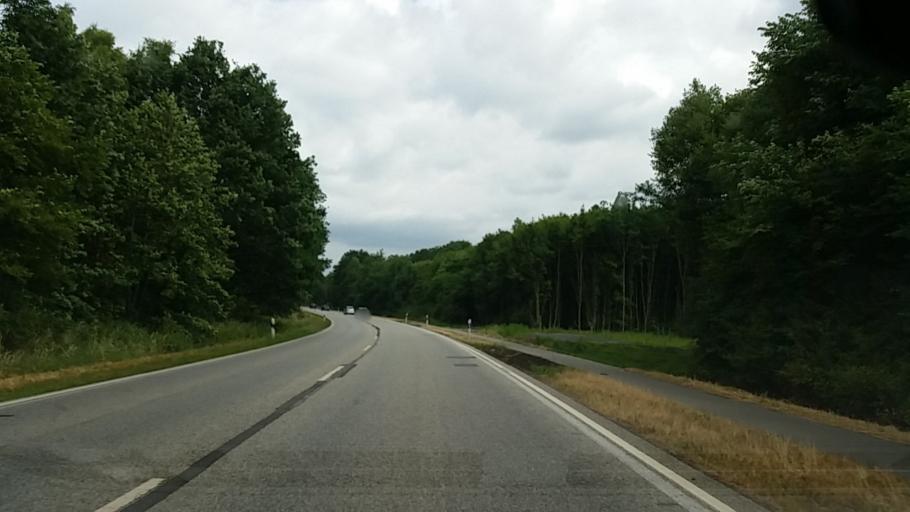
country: DE
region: Schleswig-Holstein
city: Kayhude
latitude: 53.7421
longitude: 10.1213
